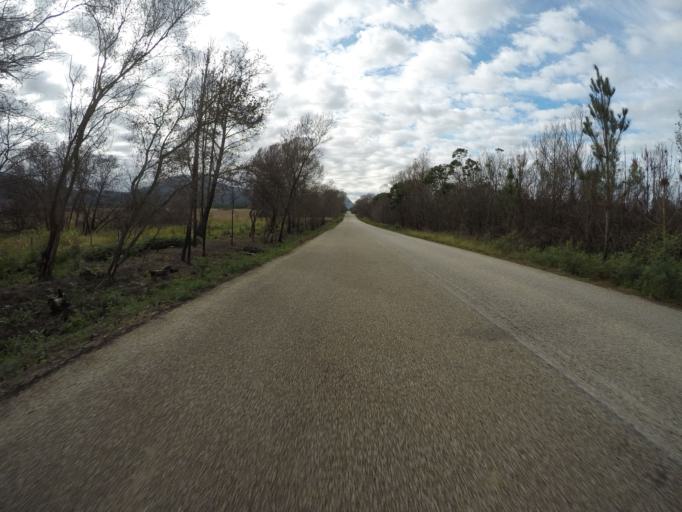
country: ZA
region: Eastern Cape
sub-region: Cacadu District Municipality
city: Kareedouw
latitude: -34.0153
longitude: 24.3249
